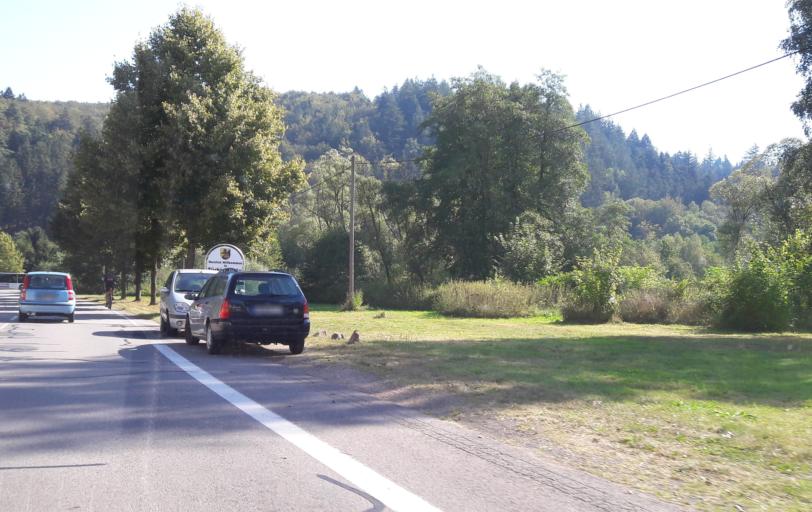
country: DE
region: Saarland
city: Nohfelden
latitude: 49.5746
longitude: 7.1101
